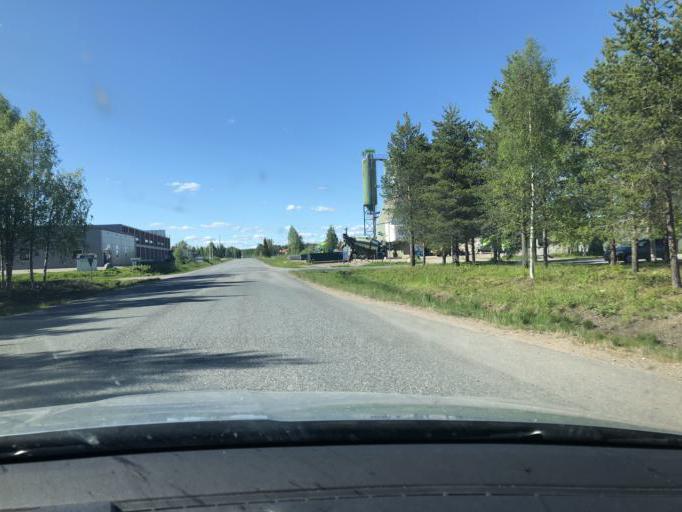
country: SE
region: Norrbotten
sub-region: Kalix Kommun
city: Kalix
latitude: 65.8477
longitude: 23.1975
